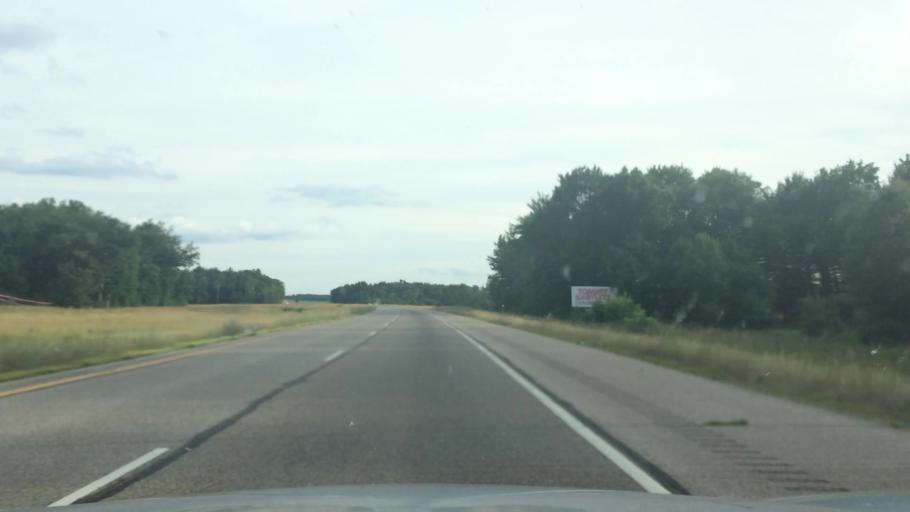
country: US
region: Wisconsin
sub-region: Waushara County
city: Wautoma
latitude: 44.1740
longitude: -89.5313
